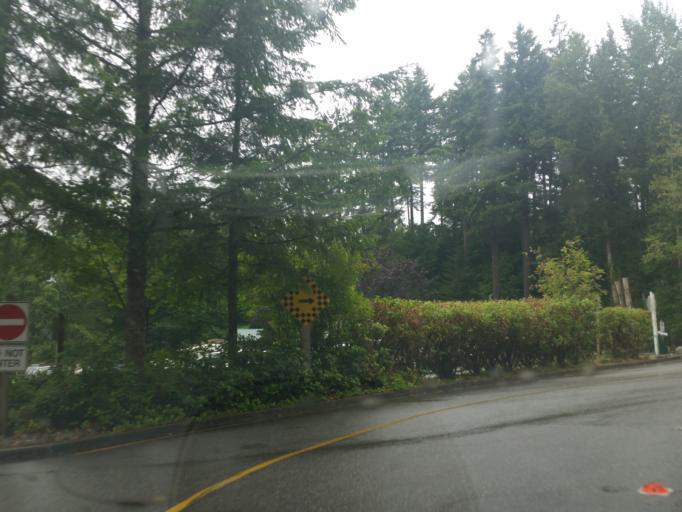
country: CA
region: British Columbia
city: Burnaby
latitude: 49.3120
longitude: -122.9254
